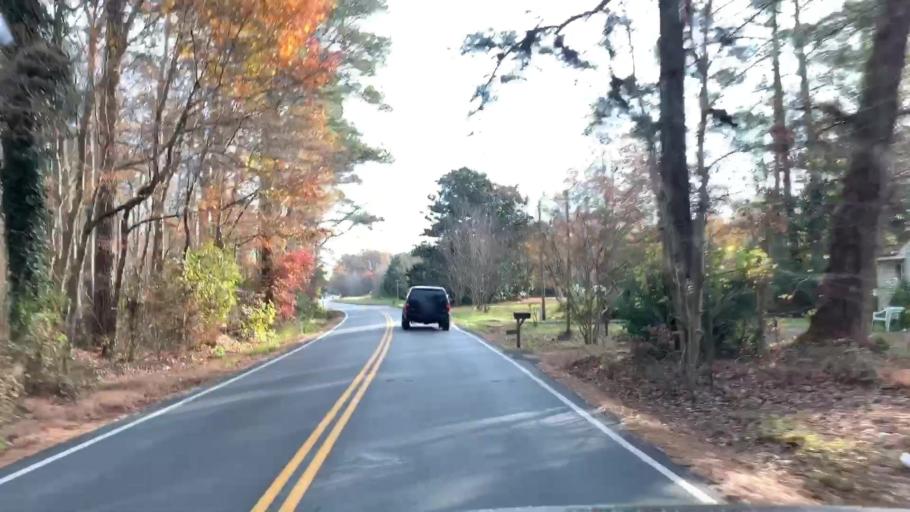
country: US
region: Virginia
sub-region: City of Virginia Beach
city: Virginia Beach
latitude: 36.6907
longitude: -76.0327
